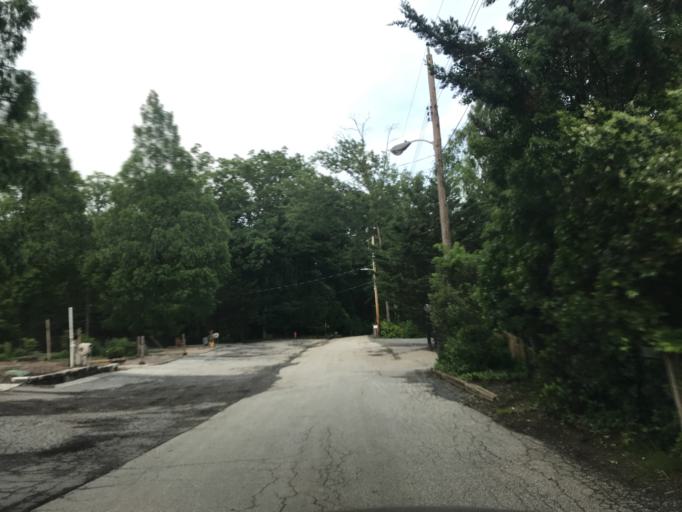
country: US
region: Maryland
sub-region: Baltimore County
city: Towson
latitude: 39.3797
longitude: -76.5952
